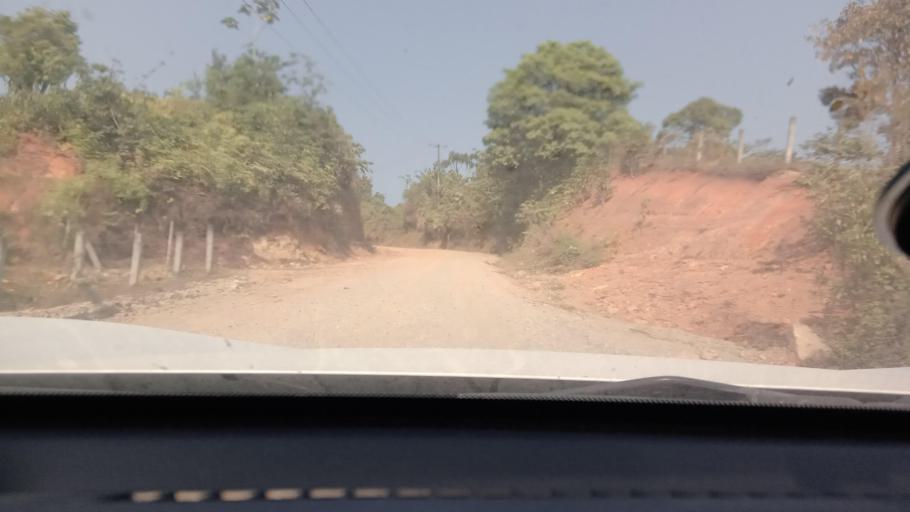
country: MX
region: Tabasco
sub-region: Huimanguillo
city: Francisco Rueda
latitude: 17.6527
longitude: -93.8856
